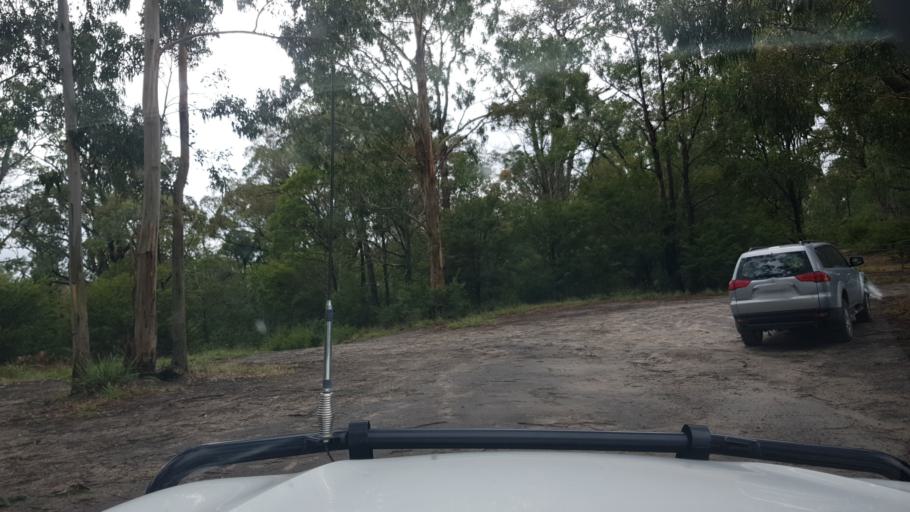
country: AU
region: Victoria
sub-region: Latrobe
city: Moe
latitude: -38.0772
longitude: 146.2396
